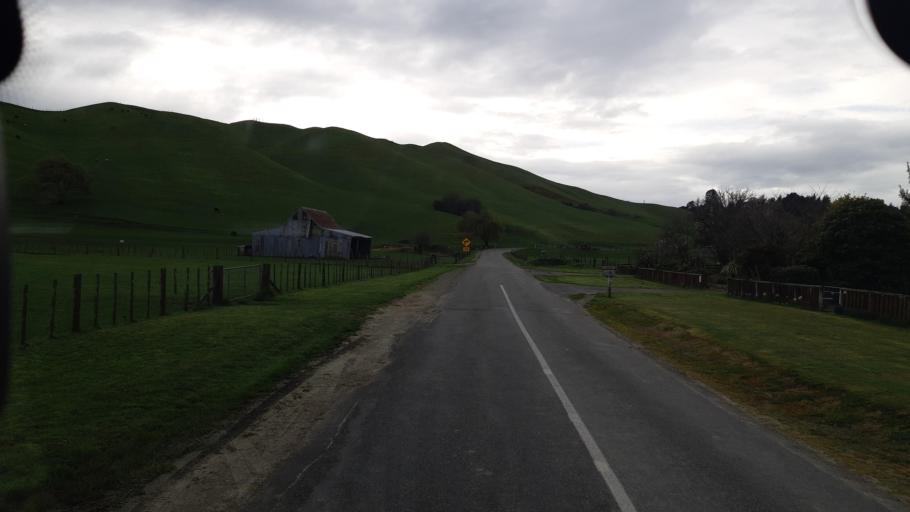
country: NZ
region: Tasman
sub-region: Tasman District
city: Motueka
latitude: -41.2765
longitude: 172.8746
